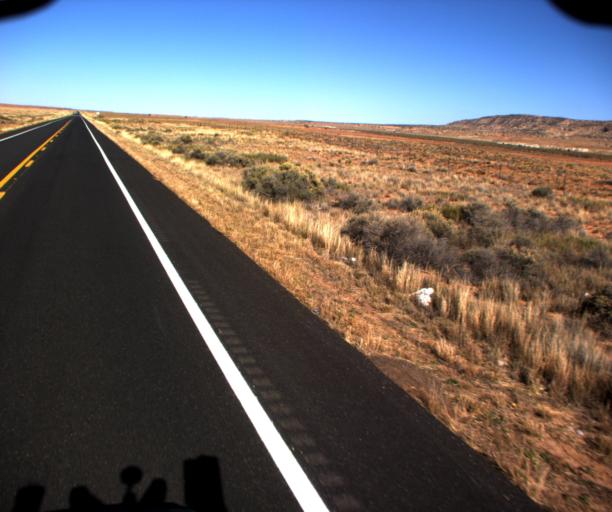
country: US
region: Arizona
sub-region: Coconino County
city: Kaibito
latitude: 36.3583
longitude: -110.9044
